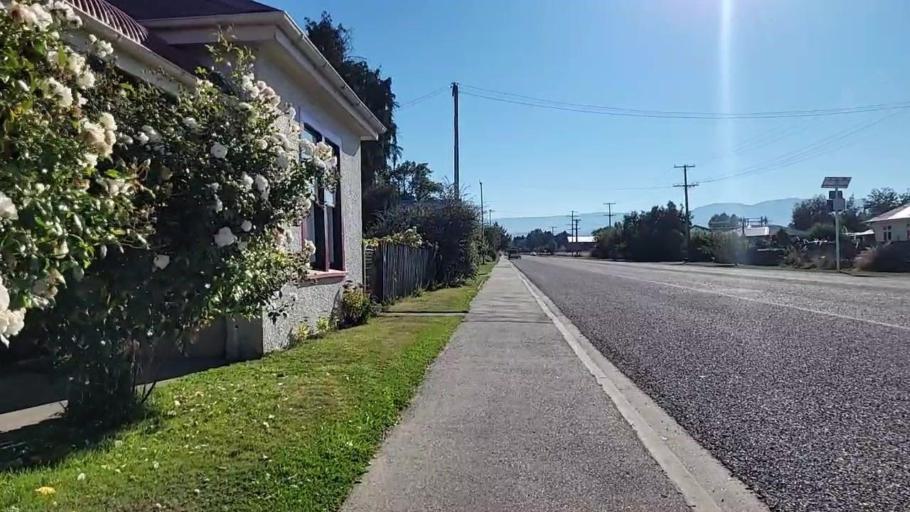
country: NZ
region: Otago
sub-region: Queenstown-Lakes District
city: Wanaka
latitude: -45.0067
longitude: 169.9131
